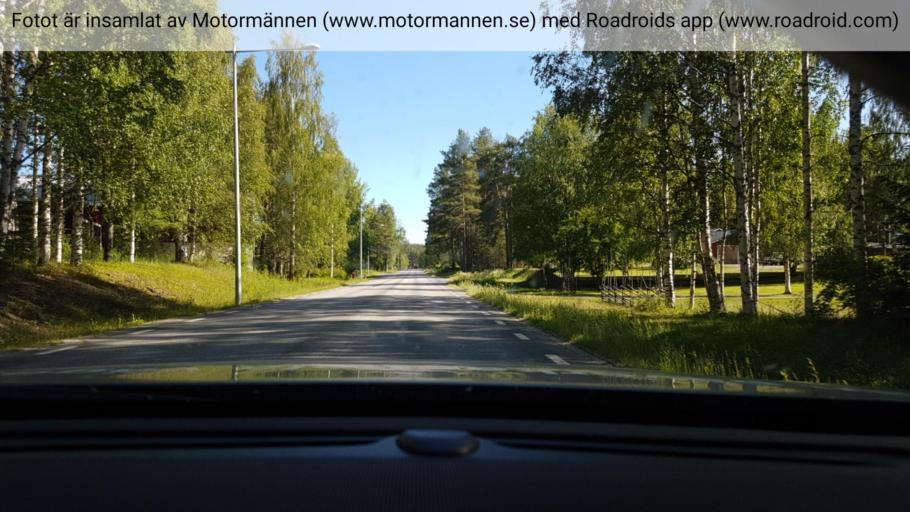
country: SE
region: Vaesterbotten
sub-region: Lycksele Kommun
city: Lycksele
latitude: 64.6205
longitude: 18.6380
